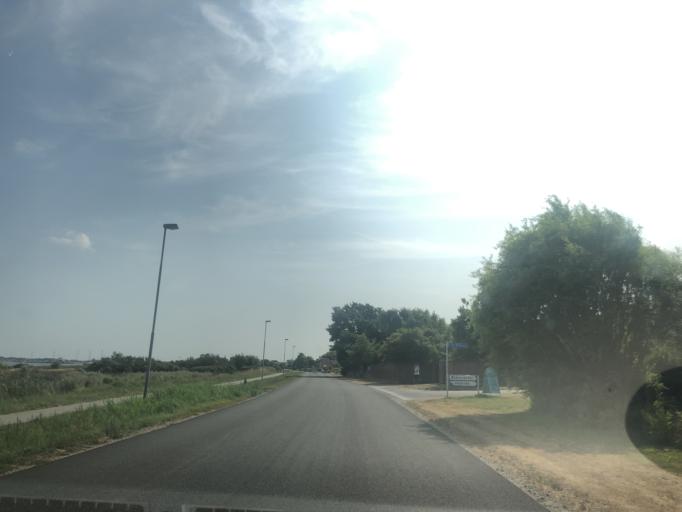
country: DK
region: North Denmark
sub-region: Morso Kommune
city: Nykobing Mors
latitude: 56.8116
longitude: 9.0220
